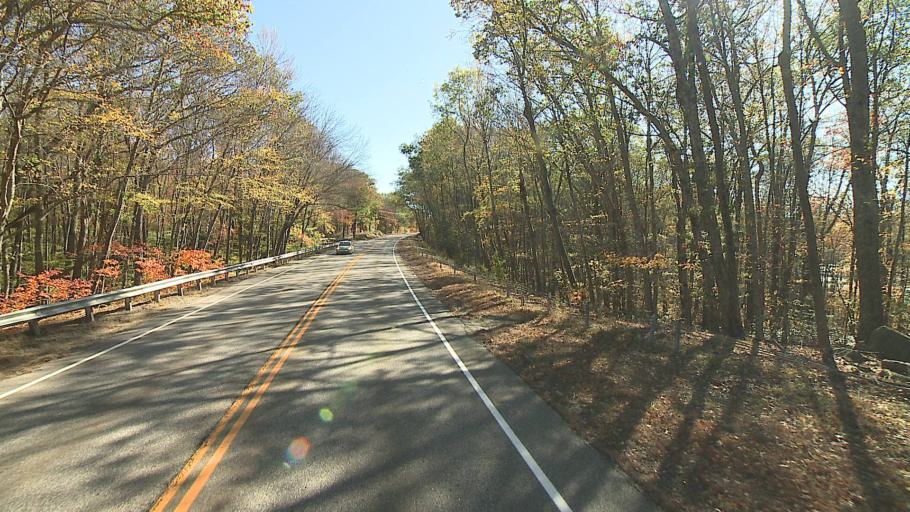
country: US
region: Connecticut
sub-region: Windham County
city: South Woodstock
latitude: 41.8690
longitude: -72.0525
